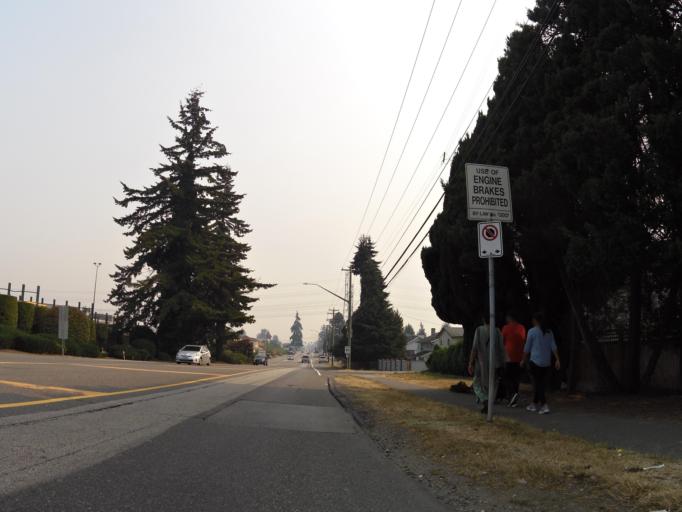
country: CA
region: British Columbia
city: Delta
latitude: 49.1483
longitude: -122.8773
